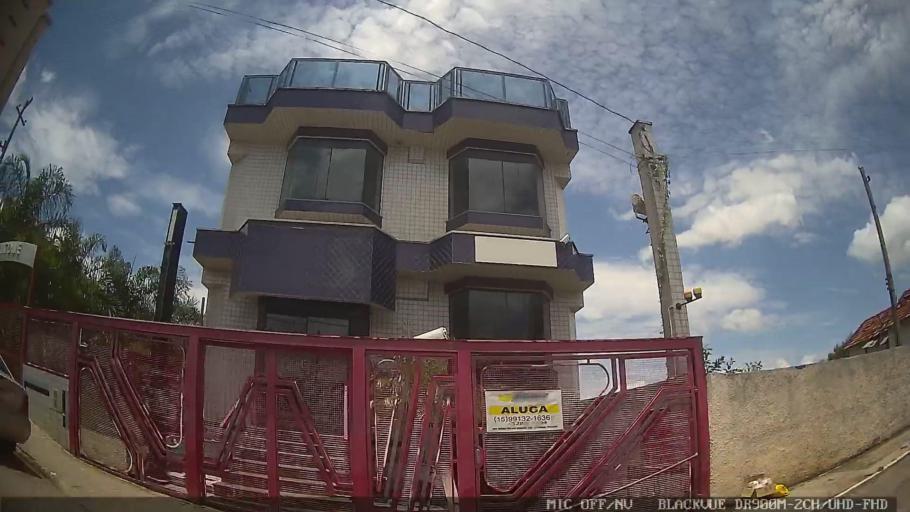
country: BR
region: Sao Paulo
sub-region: Laranjal Paulista
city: Laranjal Paulista
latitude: -23.0446
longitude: -47.8349
